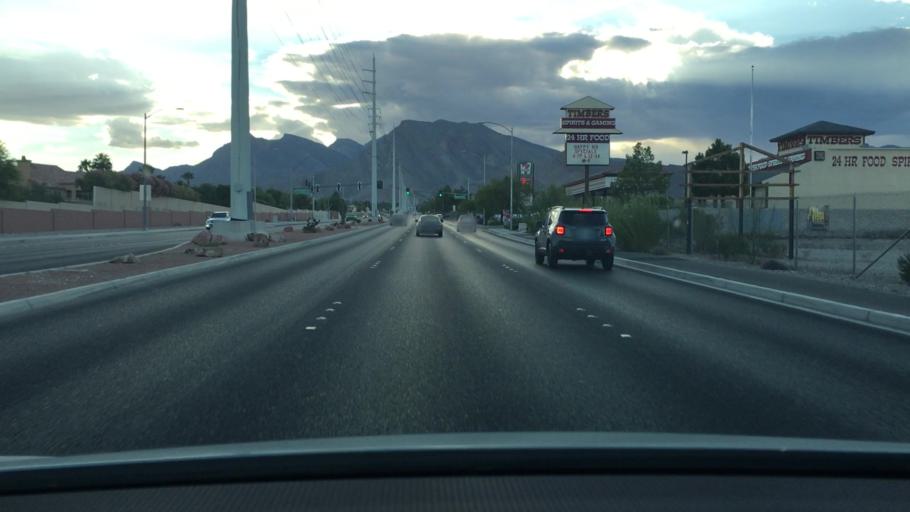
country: US
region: Nevada
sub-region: Clark County
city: Summerlin South
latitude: 36.2187
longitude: -115.2953
